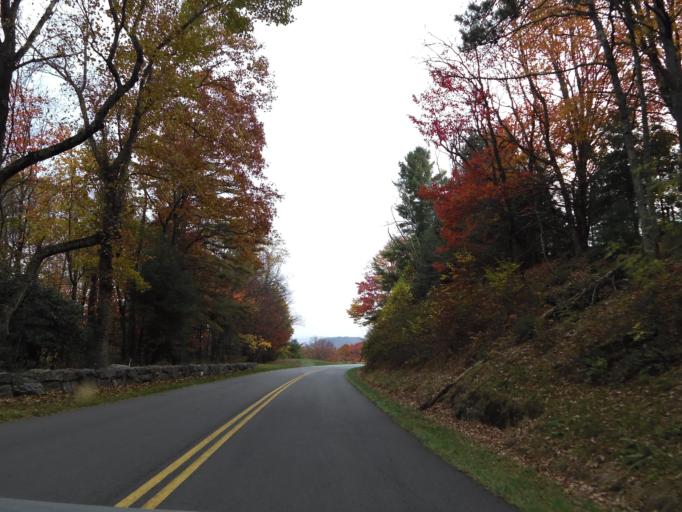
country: US
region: North Carolina
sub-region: Alleghany County
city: Sparta
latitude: 36.4127
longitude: -81.1952
